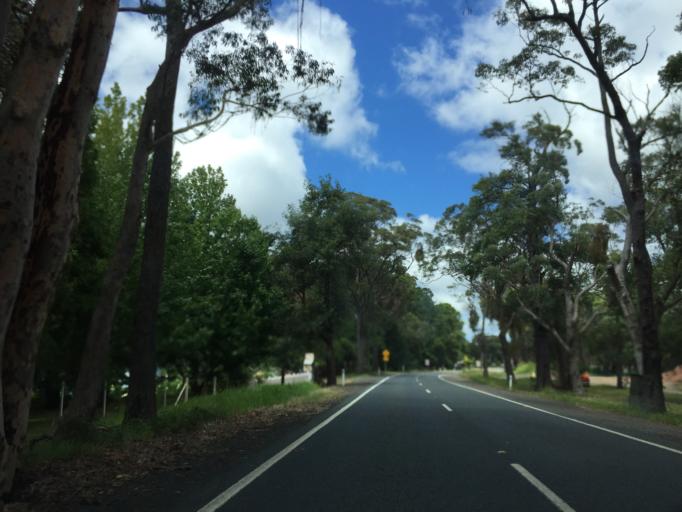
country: AU
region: New South Wales
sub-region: Blue Mountains Municipality
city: Hazelbrook
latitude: -33.4997
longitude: 150.5112
